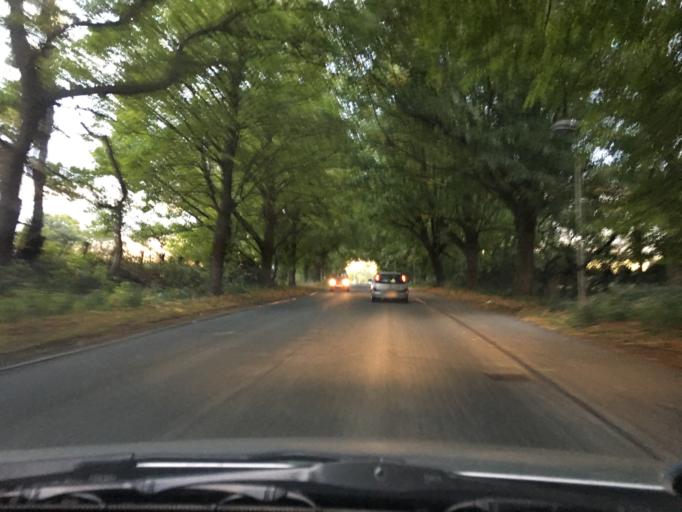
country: DE
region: Schleswig-Holstein
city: Altenholz
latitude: 54.3846
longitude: 10.1484
